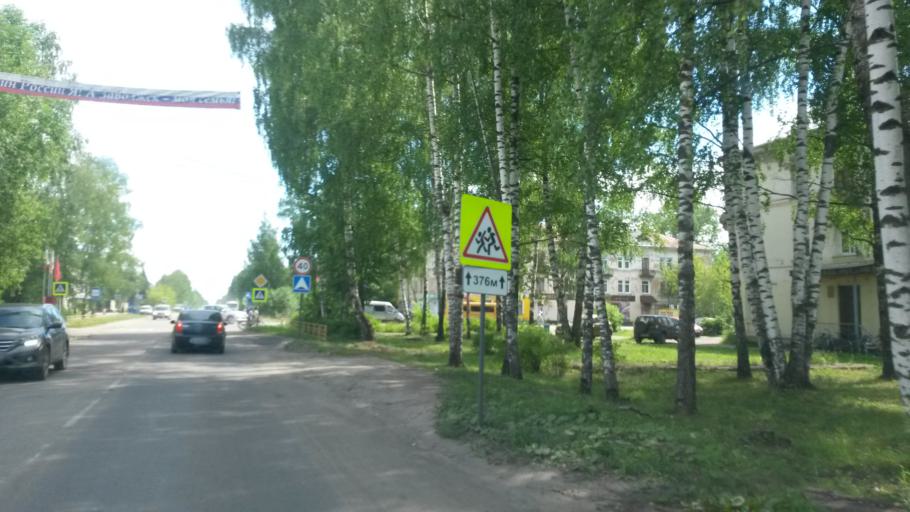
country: RU
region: Ivanovo
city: Zavolzhsk
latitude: 57.4923
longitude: 42.1368
